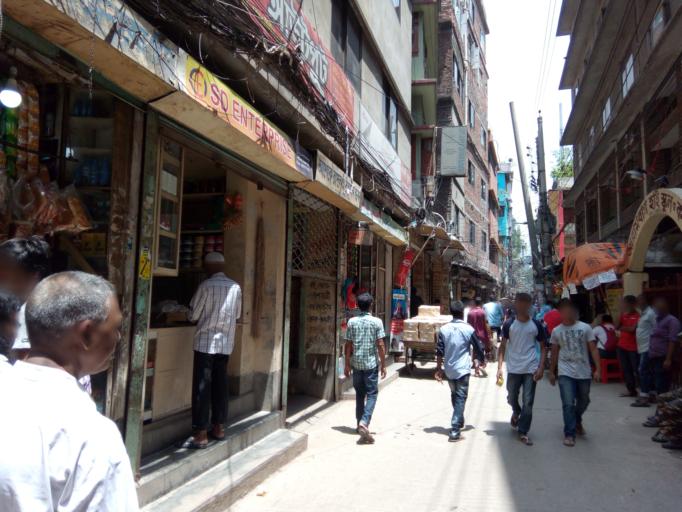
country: BD
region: Dhaka
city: Paltan
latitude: 23.7319
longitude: 90.4188
